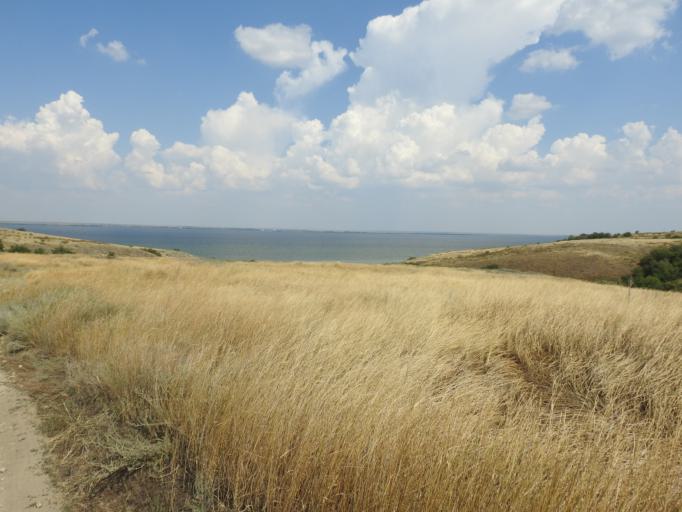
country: RU
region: Saratov
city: Rovnoye
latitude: 50.4920
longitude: 45.7952
